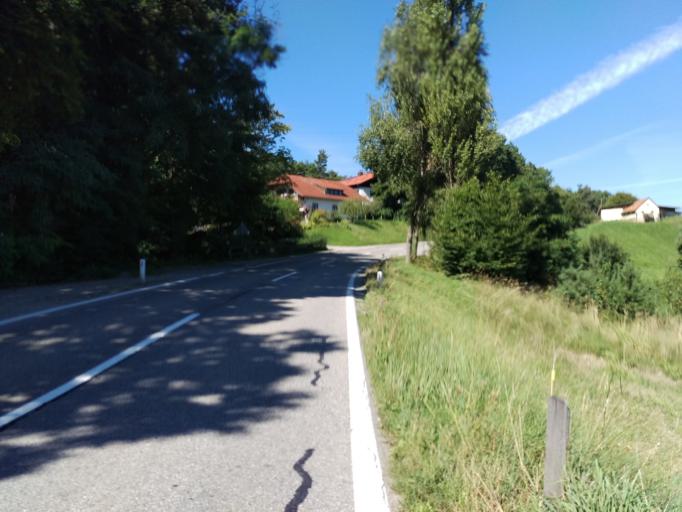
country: AT
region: Styria
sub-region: Politischer Bezirk Graz-Umgebung
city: Eggersdorf bei Graz
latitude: 47.0867
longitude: 15.5767
